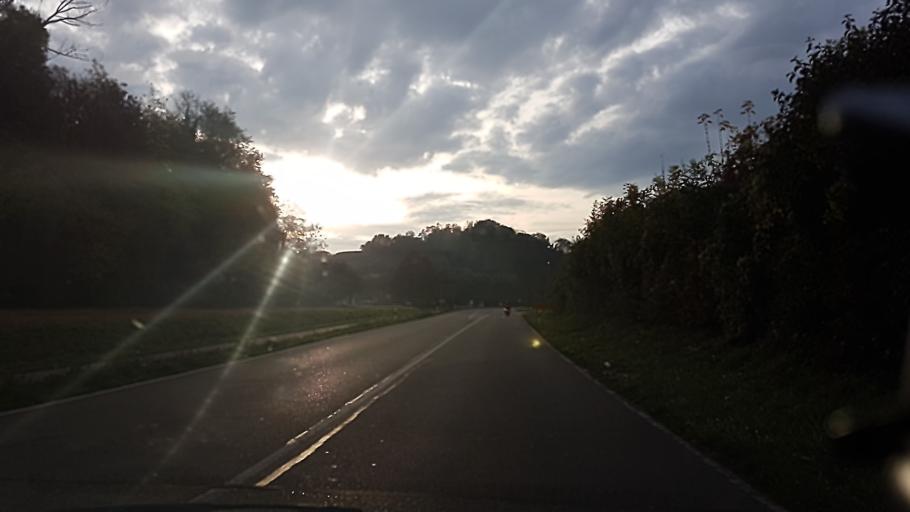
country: DE
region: Baden-Wuerttemberg
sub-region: Freiburg Region
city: Riegel
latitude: 48.1487
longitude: 7.7419
